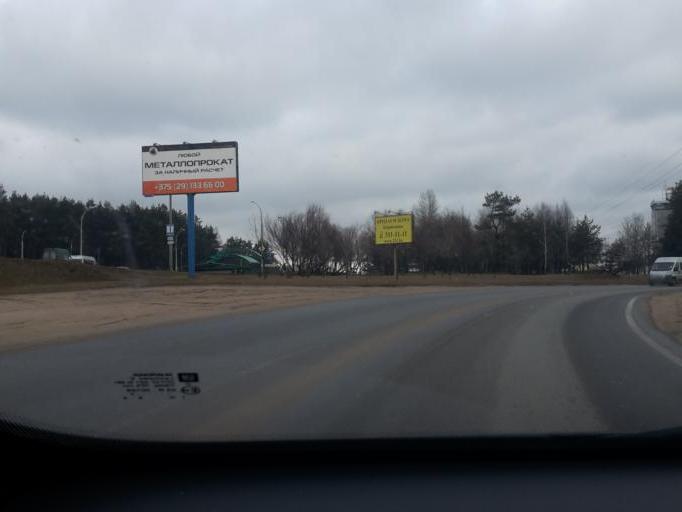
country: BY
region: Minsk
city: Borovlyany
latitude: 53.9235
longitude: 27.6811
